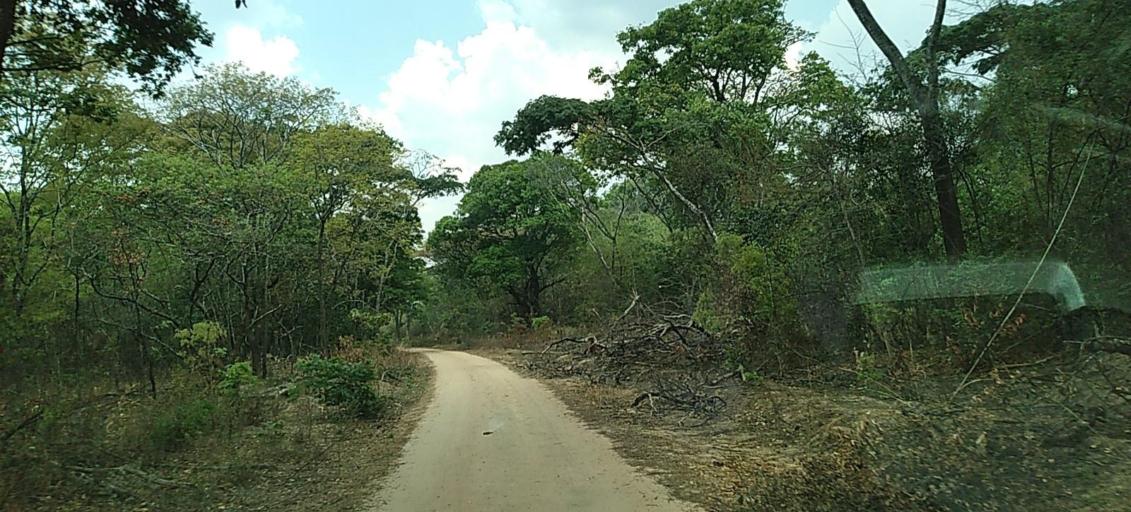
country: ZM
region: Copperbelt
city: Chingola
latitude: -12.7546
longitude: 27.7139
